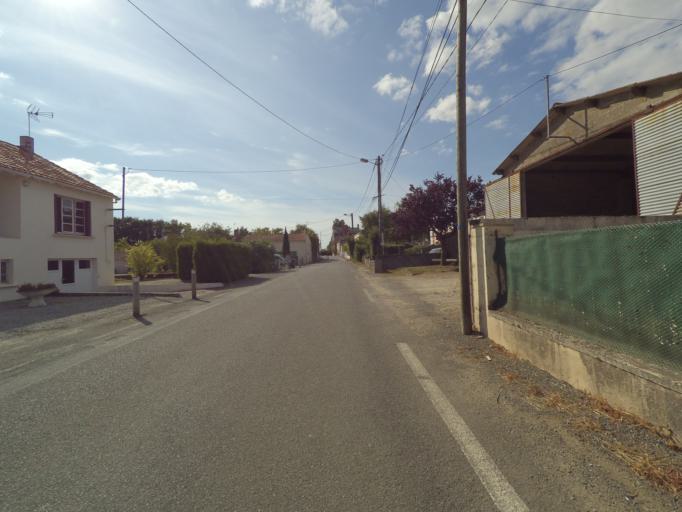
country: FR
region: Pays de la Loire
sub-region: Departement de la Loire-Atlantique
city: Vieillevigne
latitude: 46.9685
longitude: -1.4232
